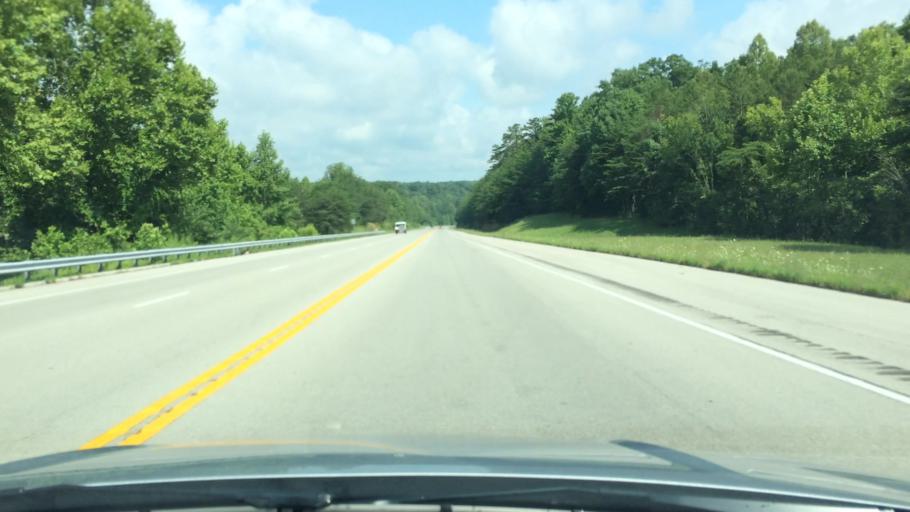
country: US
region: Kentucky
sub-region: McCreary County
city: Whitley City
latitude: 36.8452
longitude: -84.4844
